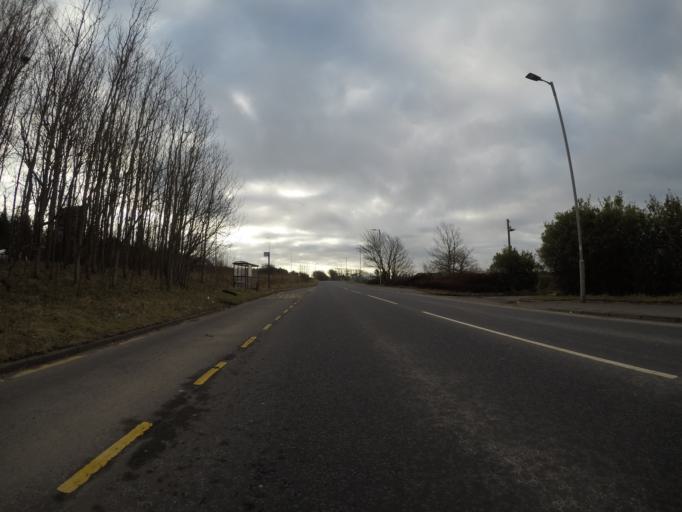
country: GB
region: Scotland
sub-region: North Ayrshire
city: Dreghorn
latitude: 55.5744
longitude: -4.6412
